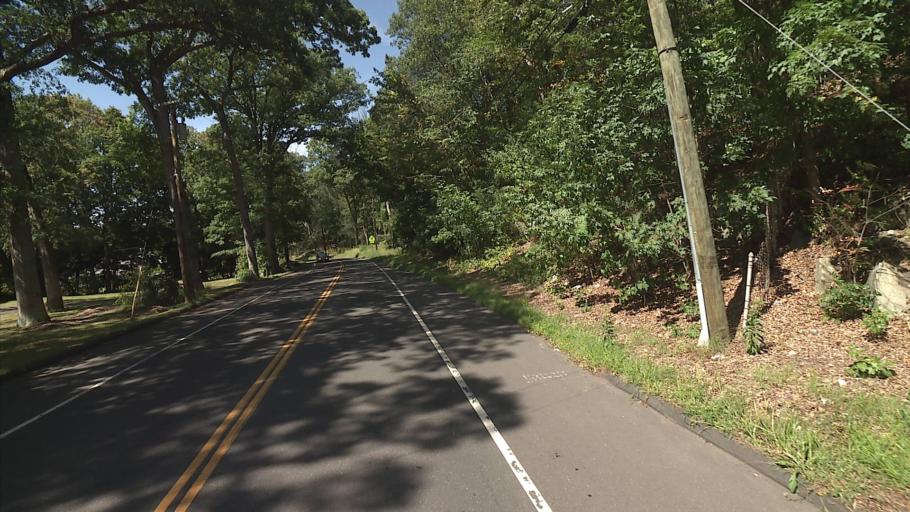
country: US
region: Connecticut
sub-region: New Haven County
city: Middlebury
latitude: 41.5262
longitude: -73.0892
